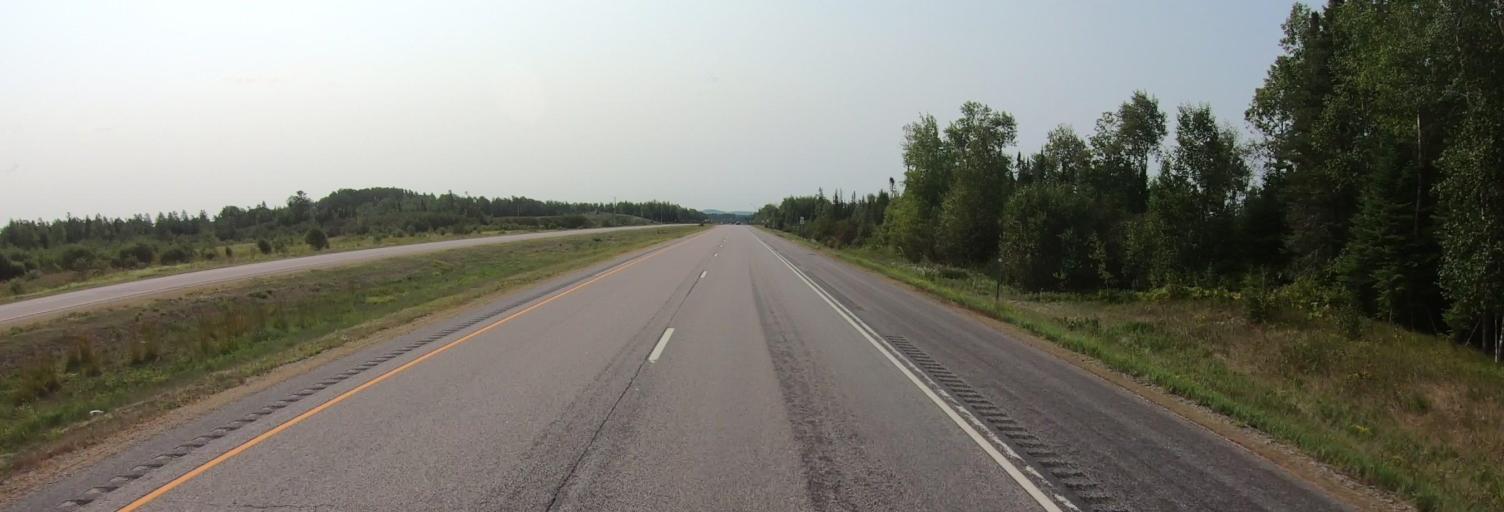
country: US
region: Minnesota
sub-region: Saint Louis County
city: Parkville
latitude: 47.6462
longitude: -92.5662
